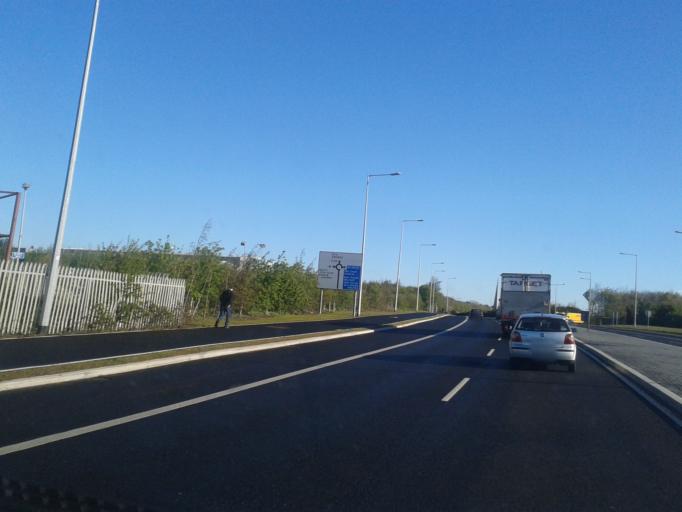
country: IE
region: Leinster
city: Kinsealy-Drinan
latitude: 53.4256
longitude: -6.2295
